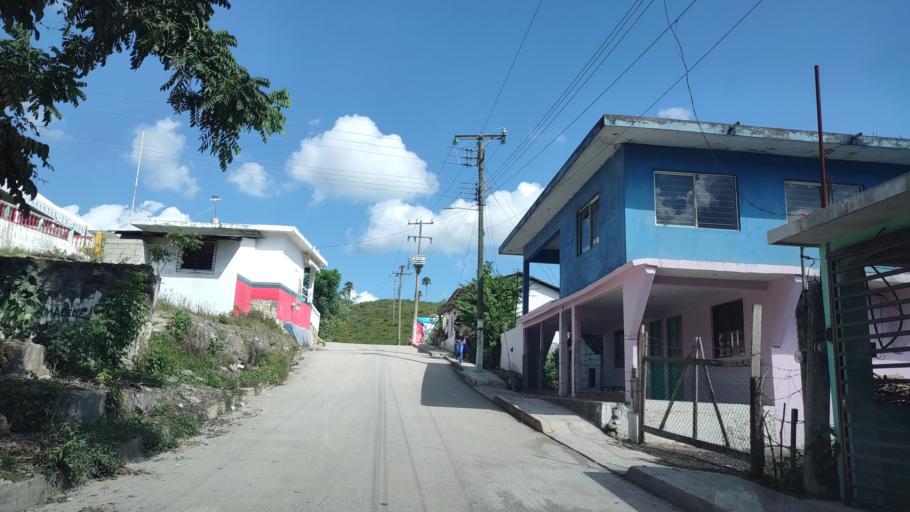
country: MM
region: Shan
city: Taunggyi
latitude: 20.5845
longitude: 97.3751
